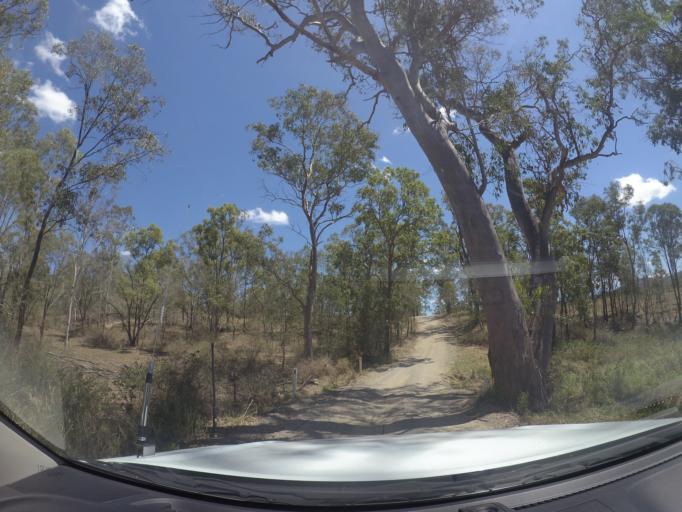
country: AU
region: Queensland
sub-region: Logan
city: North Maclean
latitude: -27.8357
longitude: 152.8700
